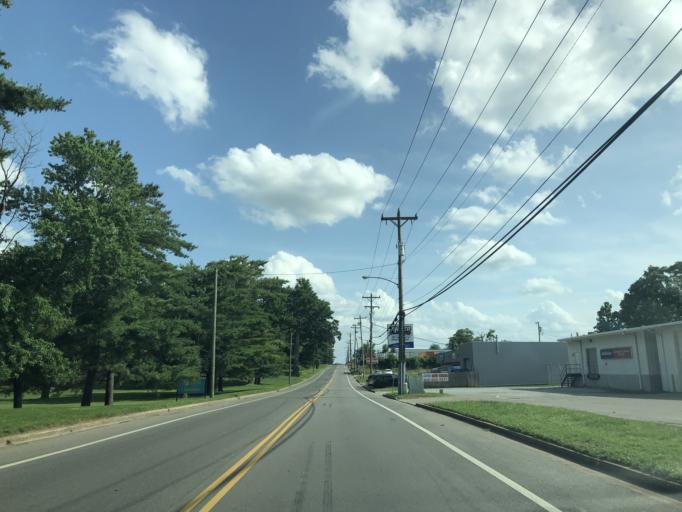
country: US
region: Tennessee
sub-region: Davidson County
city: Nashville
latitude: 36.1348
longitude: -86.7413
